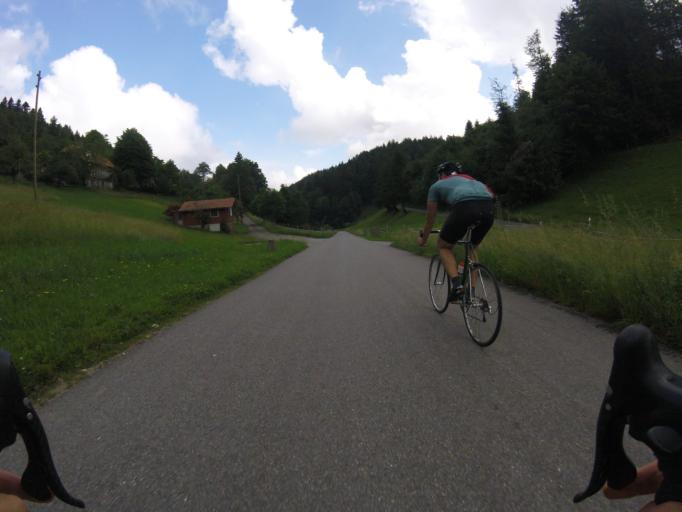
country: CH
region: Bern
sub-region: Emmental District
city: Krauchthal
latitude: 46.9833
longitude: 7.5824
